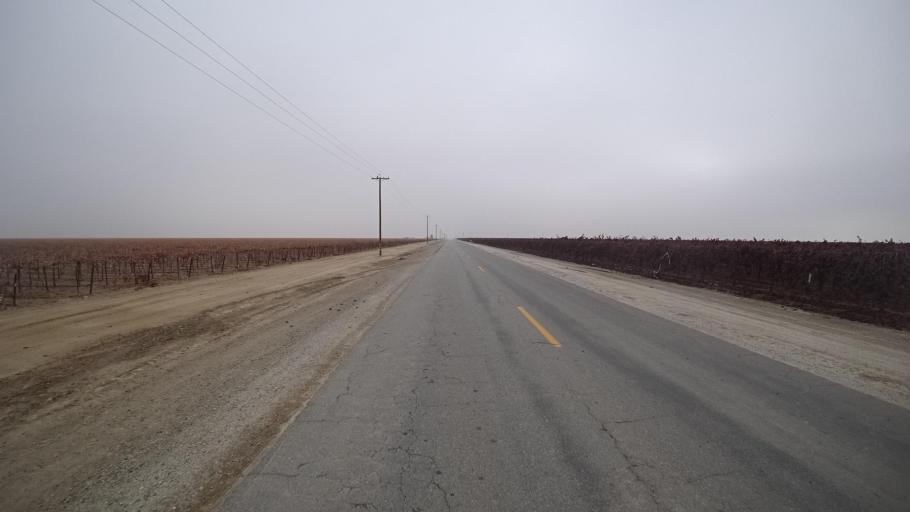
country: US
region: California
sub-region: Kern County
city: Greenfield
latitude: 35.0942
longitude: -119.1608
